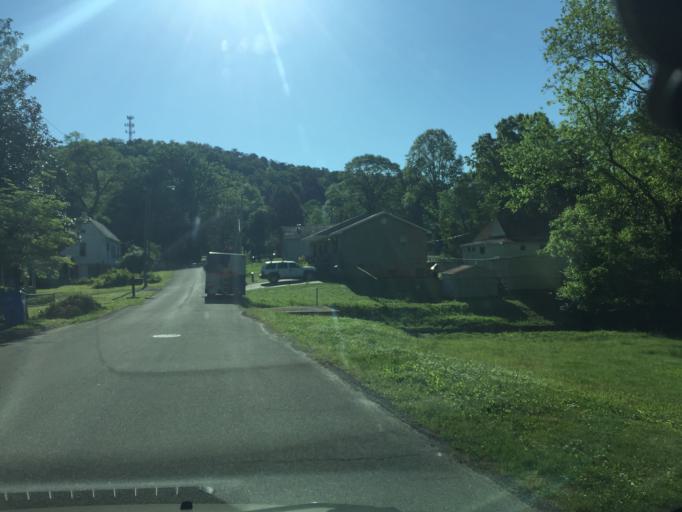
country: US
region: Tennessee
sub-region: Hamilton County
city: Lookout Mountain
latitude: 34.9897
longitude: -85.3288
